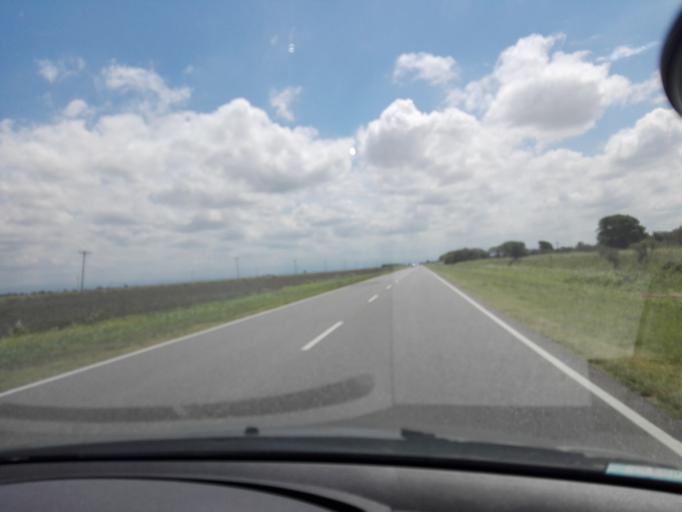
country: AR
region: Cordoba
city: Toledo
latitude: -31.6489
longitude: -64.1199
